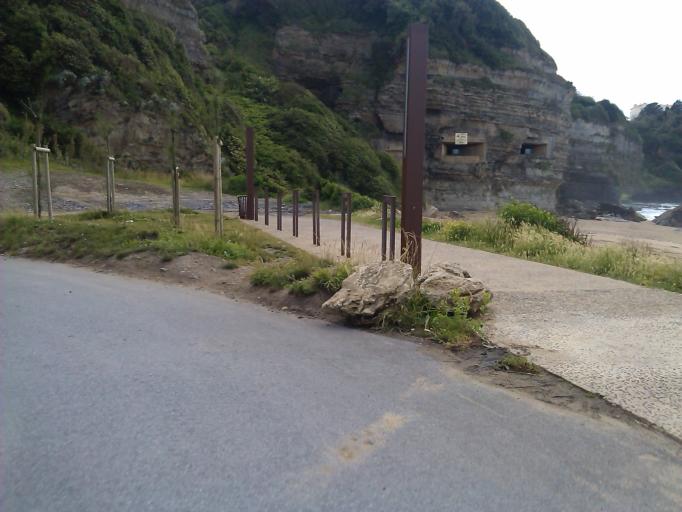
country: FR
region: Aquitaine
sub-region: Departement des Pyrenees-Atlantiques
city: Biarritz
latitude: 43.4941
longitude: -1.5463
